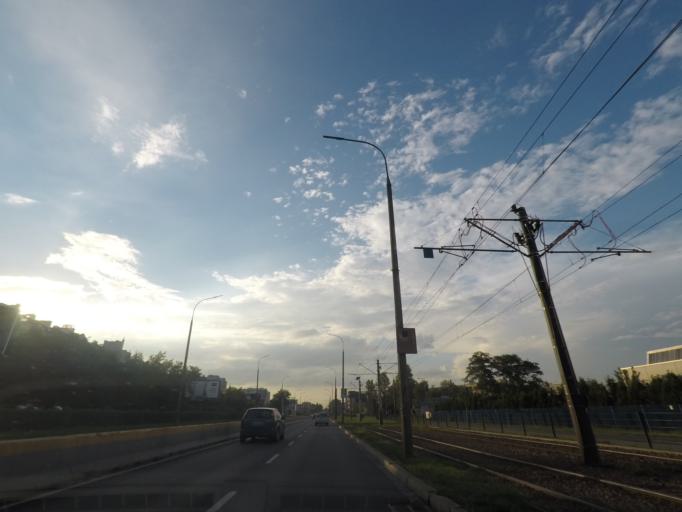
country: PL
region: Lesser Poland Voivodeship
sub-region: Krakow
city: Krakow
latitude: 50.0302
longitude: 19.9735
